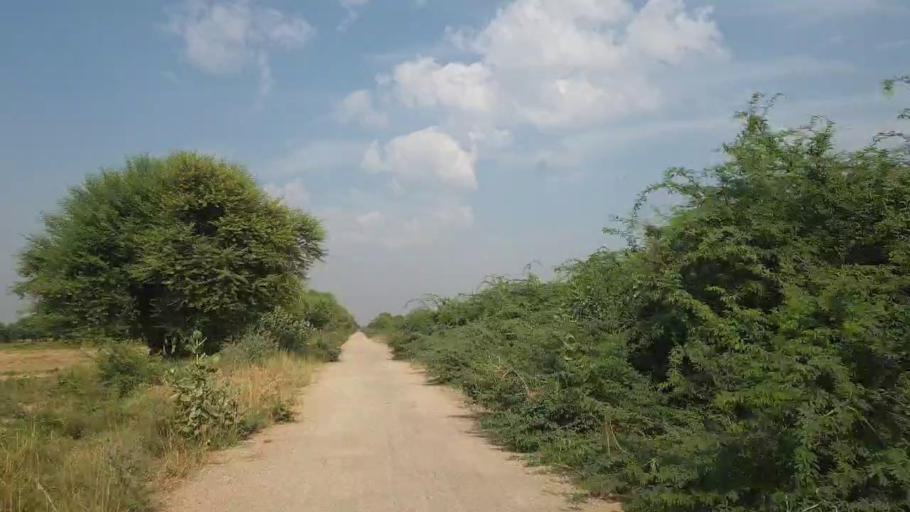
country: PK
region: Sindh
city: Digri
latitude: 25.0181
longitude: 69.0681
